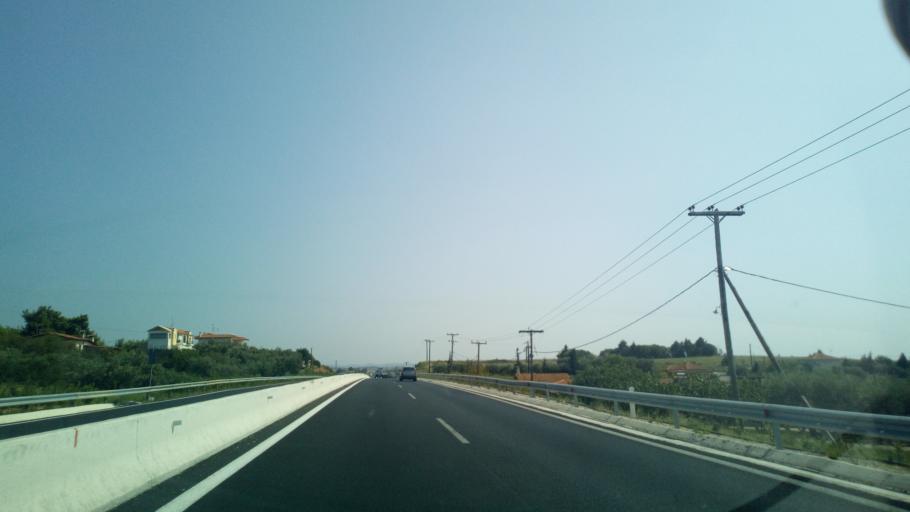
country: GR
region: Central Macedonia
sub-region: Nomos Chalkidikis
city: Nea Potidhaia
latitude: 40.1541
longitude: 23.3532
